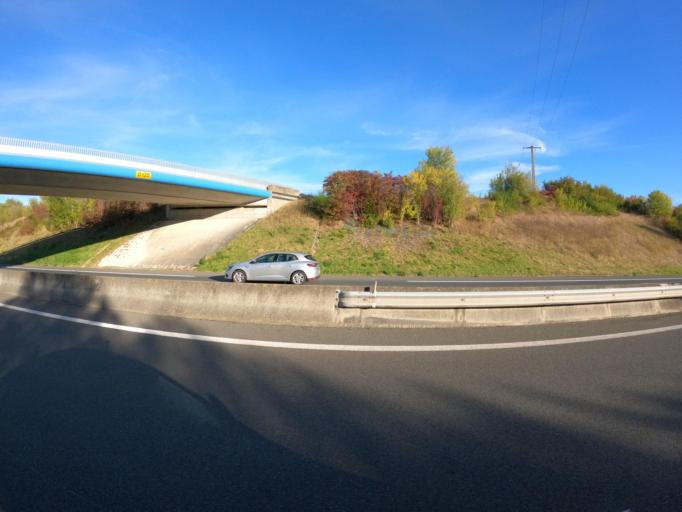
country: FR
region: Pays de la Loire
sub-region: Departement de Maine-et-Loire
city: Beaulieu-sur-Layon
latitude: 47.2984
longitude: -0.6097
